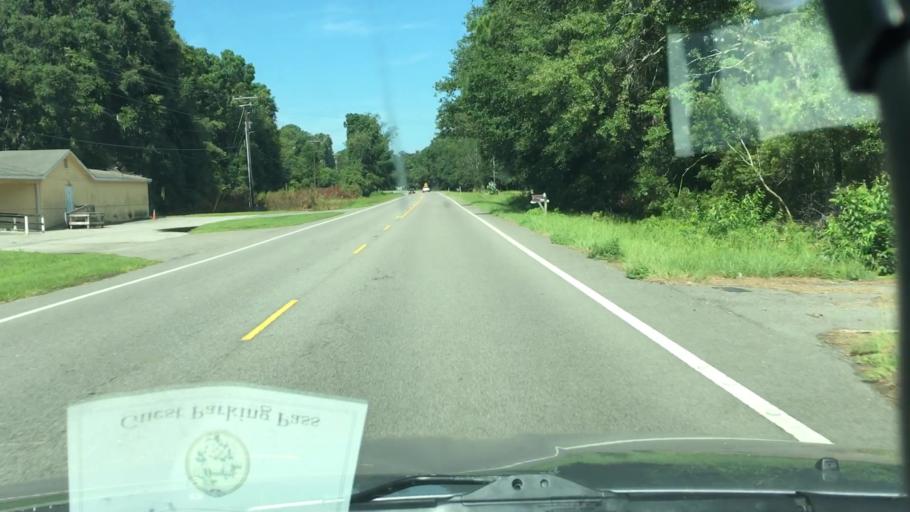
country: US
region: South Carolina
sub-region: Beaufort County
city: Beaufort
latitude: 32.4123
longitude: -80.5160
